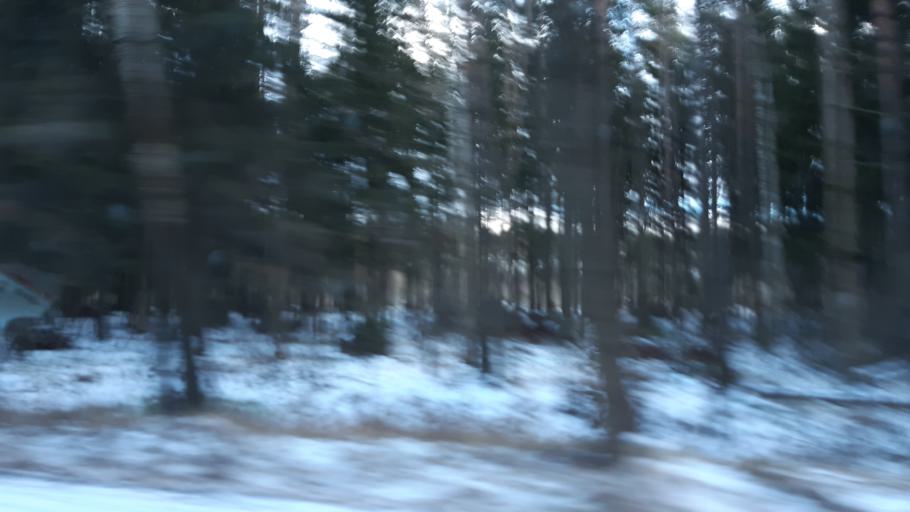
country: RU
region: Moskovskaya
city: Noginsk
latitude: 55.9357
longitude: 38.5462
